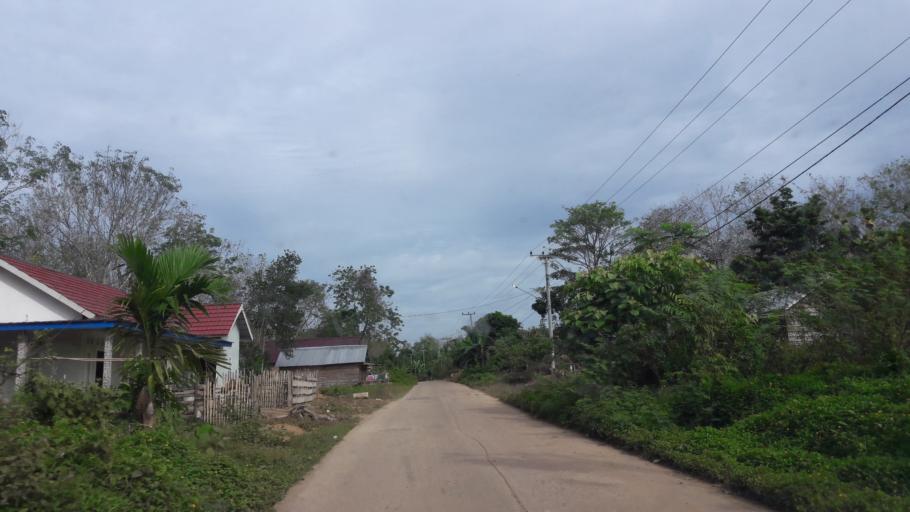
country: ID
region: South Sumatra
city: Gunungmegang Dalam
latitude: -3.2870
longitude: 103.7211
